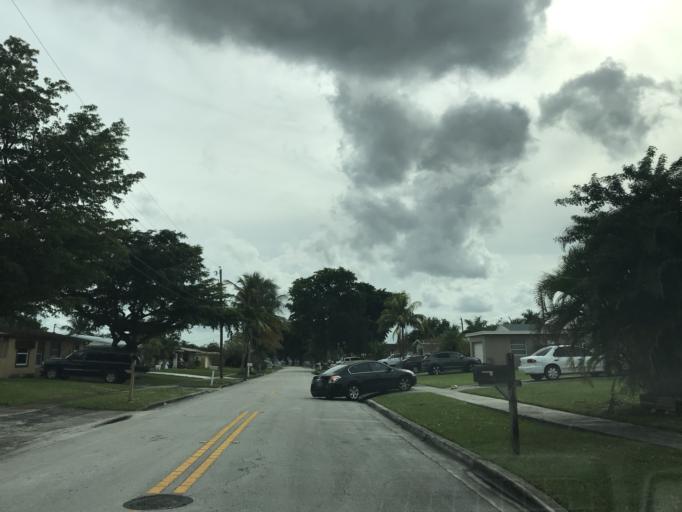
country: US
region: Florida
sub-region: Broward County
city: Margate
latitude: 26.2566
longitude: -80.2098
